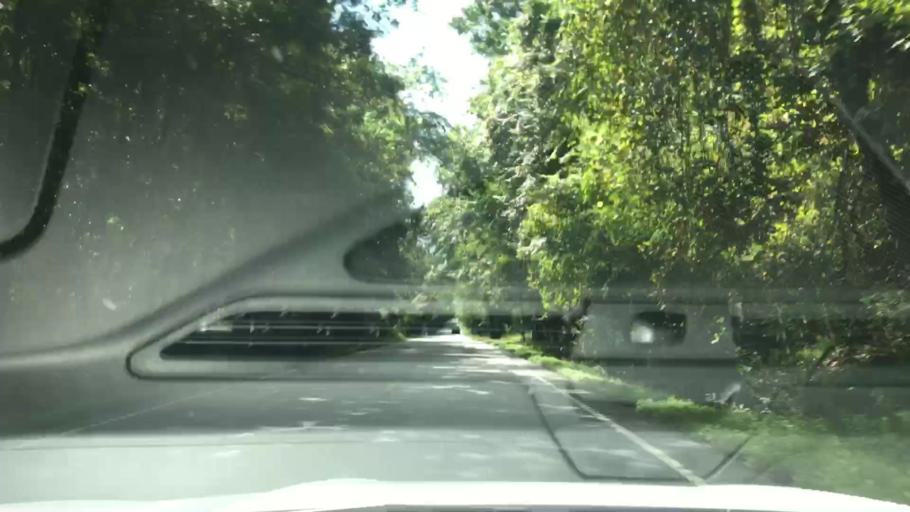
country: US
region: South Carolina
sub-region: Berkeley County
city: Hanahan
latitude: 32.8775
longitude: -80.0980
